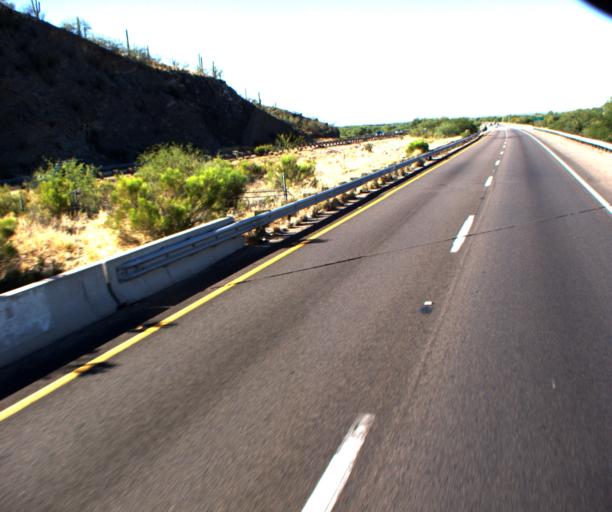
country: US
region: Arizona
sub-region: Pima County
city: Drexel Heights
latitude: 32.1066
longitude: -110.9930
